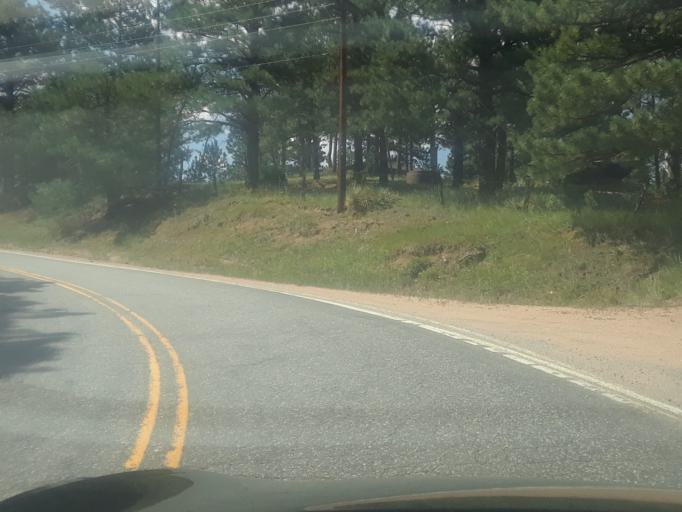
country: US
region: Colorado
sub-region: Boulder County
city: Boulder
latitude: 40.0485
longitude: -105.3354
